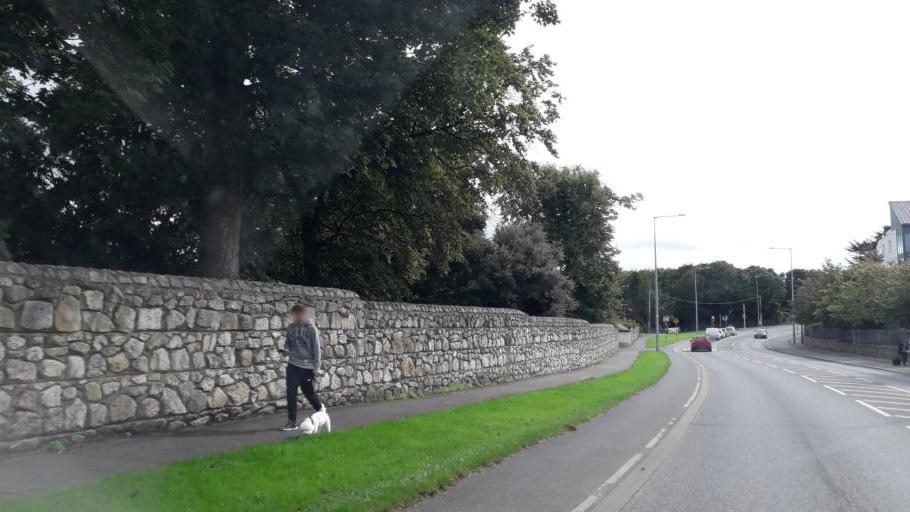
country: IE
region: Leinster
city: Cabinteely
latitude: 53.2660
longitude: -6.1484
